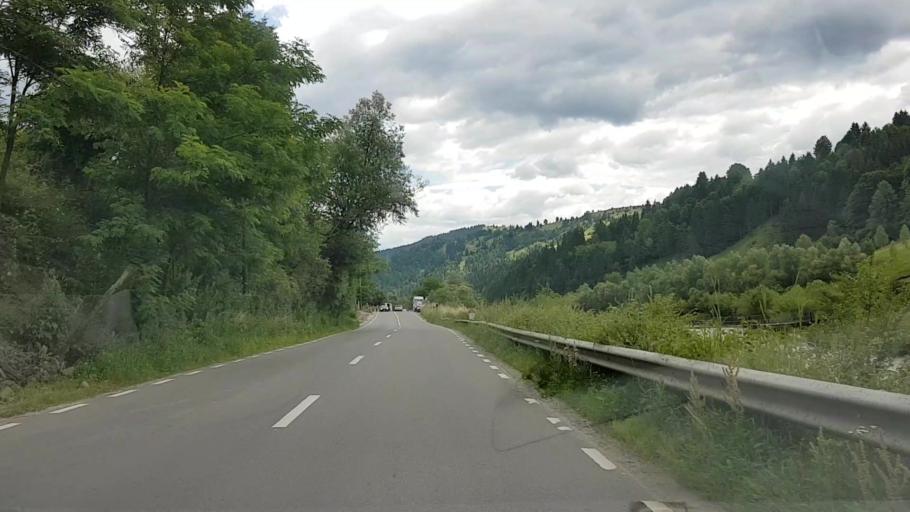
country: RO
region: Neamt
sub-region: Comuna Farcasa
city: Farcasa
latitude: 47.1658
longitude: 25.8079
